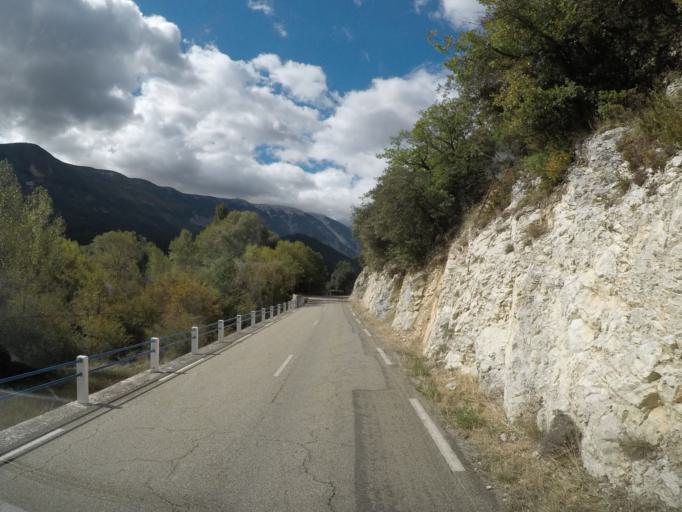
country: FR
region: Provence-Alpes-Cote d'Azur
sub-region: Departement du Vaucluse
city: Sault
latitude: 44.1834
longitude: 5.3685
